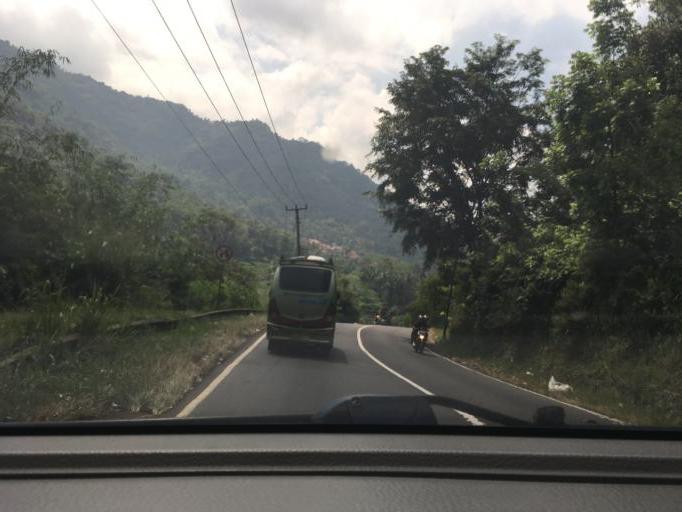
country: ID
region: West Java
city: Wage Cibahayu
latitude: -7.1162
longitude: 108.1221
